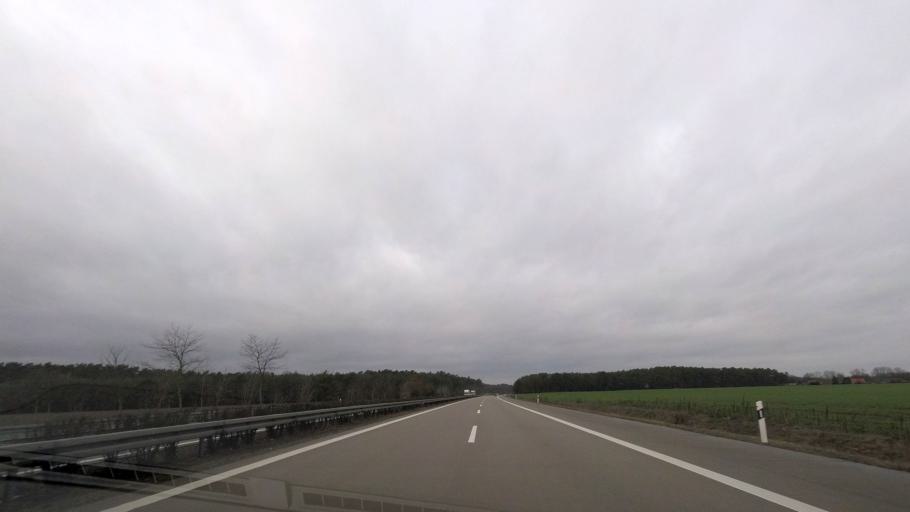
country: DE
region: Mecklenburg-Vorpommern
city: Rastow
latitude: 53.4373
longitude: 11.3889
